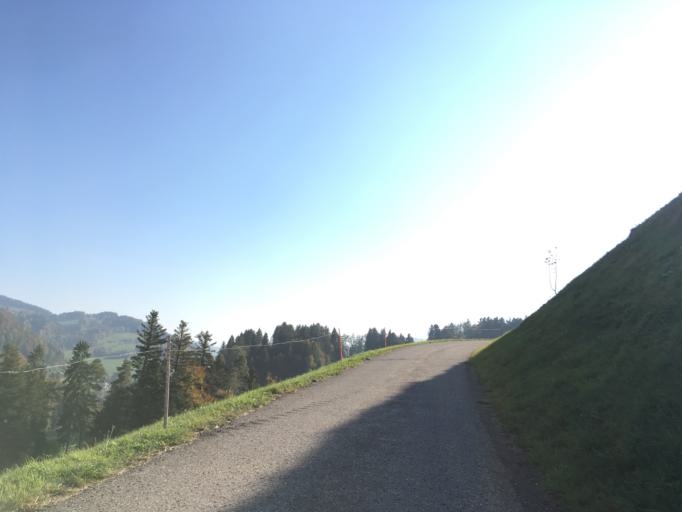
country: CH
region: Saint Gallen
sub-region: Wahlkreis Toggenburg
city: Mogelsberg
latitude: 47.3578
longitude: 9.1237
